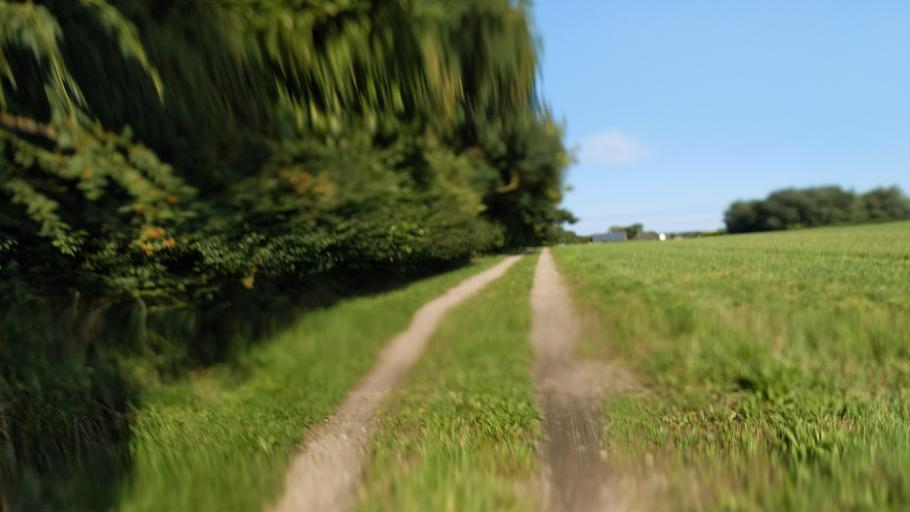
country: DE
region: Schleswig-Holstein
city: Travemuende
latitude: 53.9614
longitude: 10.9348
